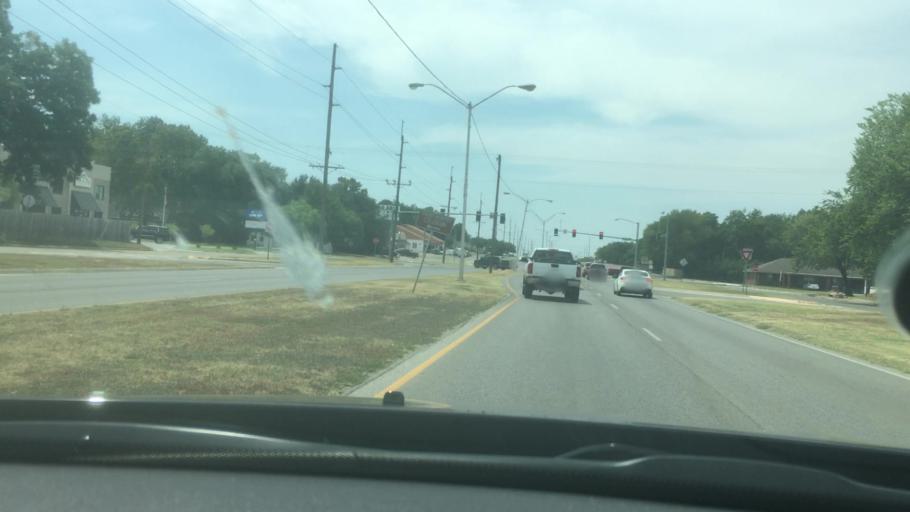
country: US
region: Oklahoma
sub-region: Carter County
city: Ardmore
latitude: 34.1722
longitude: -97.1434
